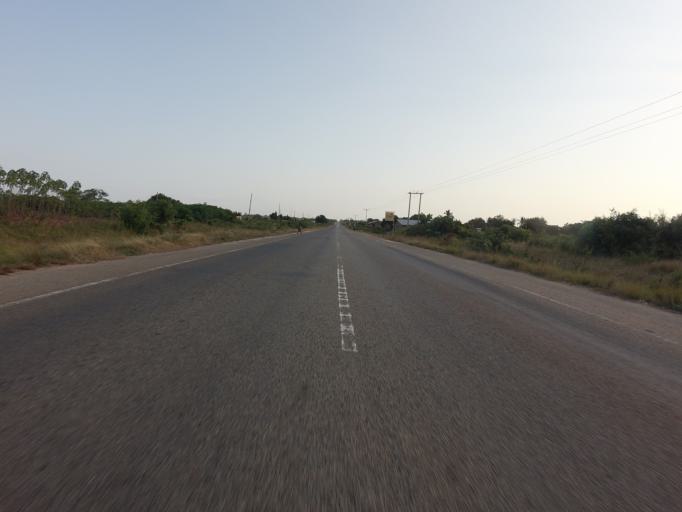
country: GH
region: Volta
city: Anloga
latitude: 6.0274
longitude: 0.6024
